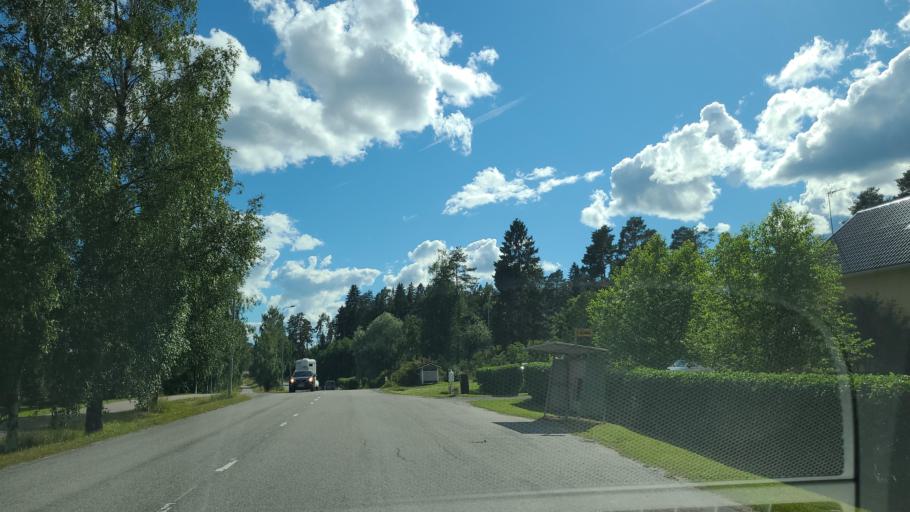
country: FI
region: Central Finland
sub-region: Jaemsae
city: Jaemsae
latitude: 61.8729
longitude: 25.2156
